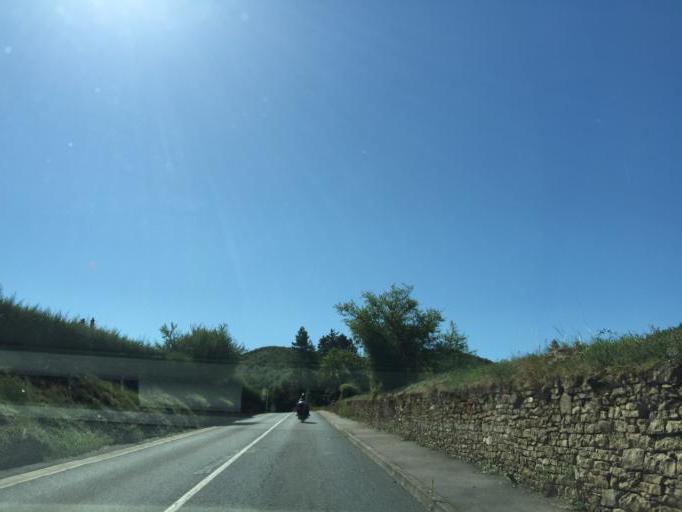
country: FR
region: Midi-Pyrenees
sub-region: Departement de l'Aveyron
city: Saint-Georges-de-Luzencon
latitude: 44.0439
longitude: 2.9045
